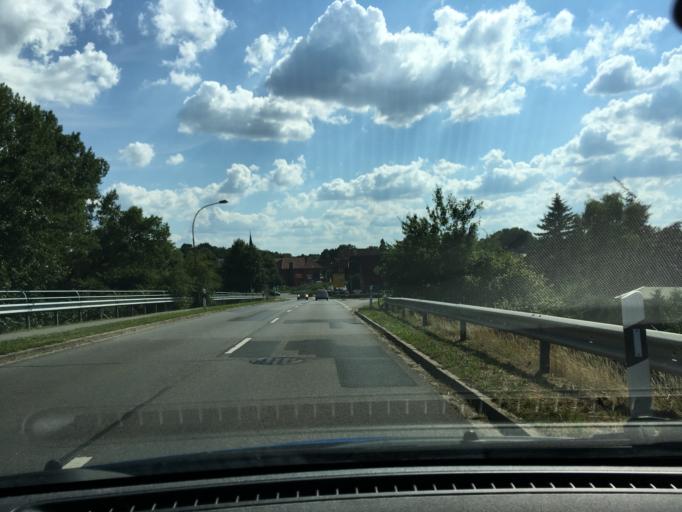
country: DE
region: Lower Saxony
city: Stelle
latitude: 53.3855
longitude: 10.1128
